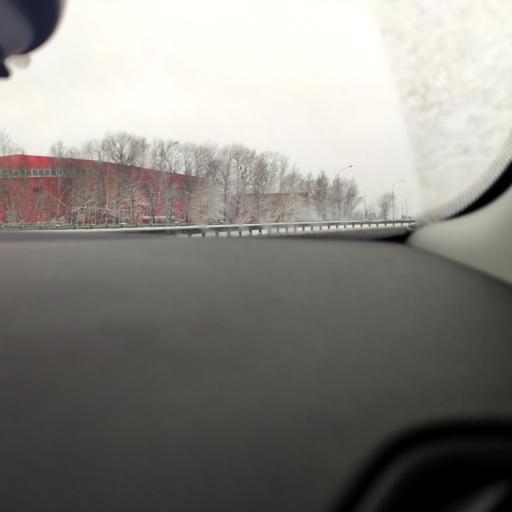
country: RU
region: Moskovskaya
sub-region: Podol'skiy Rayon
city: Podol'sk
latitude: 55.4354
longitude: 37.6140
